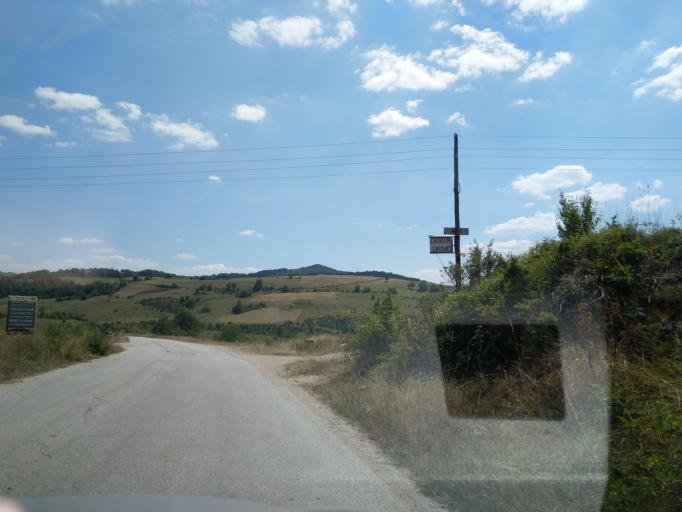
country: RS
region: Central Serbia
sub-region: Zlatiborski Okrug
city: Nova Varos
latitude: 43.4405
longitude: 19.9562
